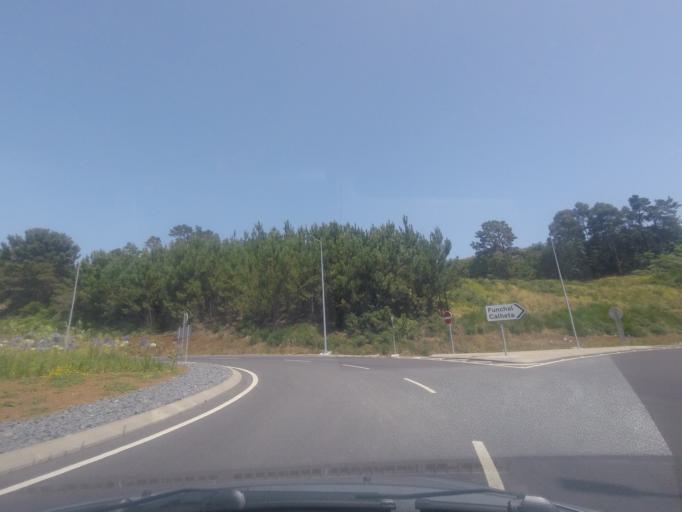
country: PT
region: Madeira
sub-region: Calheta
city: Faja da Ovelha
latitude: 32.7770
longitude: -17.2199
